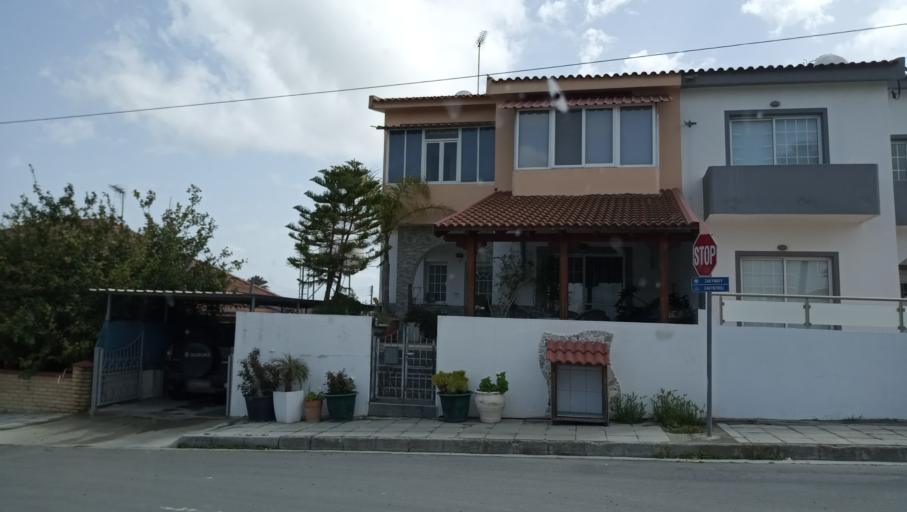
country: CY
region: Lefkosia
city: Dali
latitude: 35.0205
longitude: 33.4244
